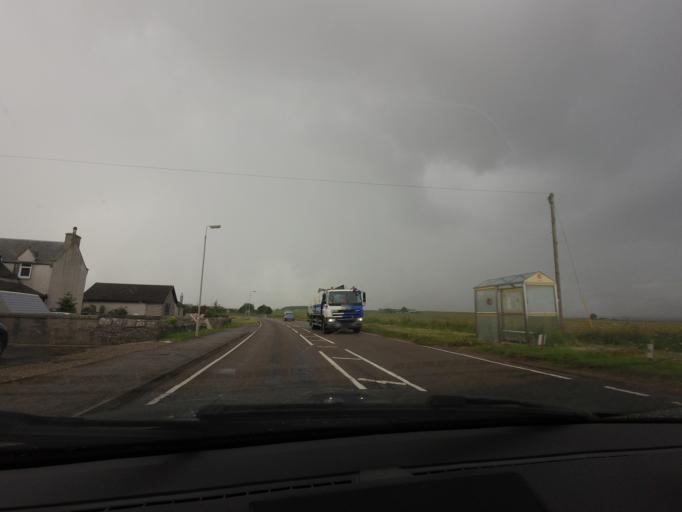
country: GB
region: Scotland
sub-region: Moray
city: Buckie
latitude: 57.6580
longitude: -2.9816
